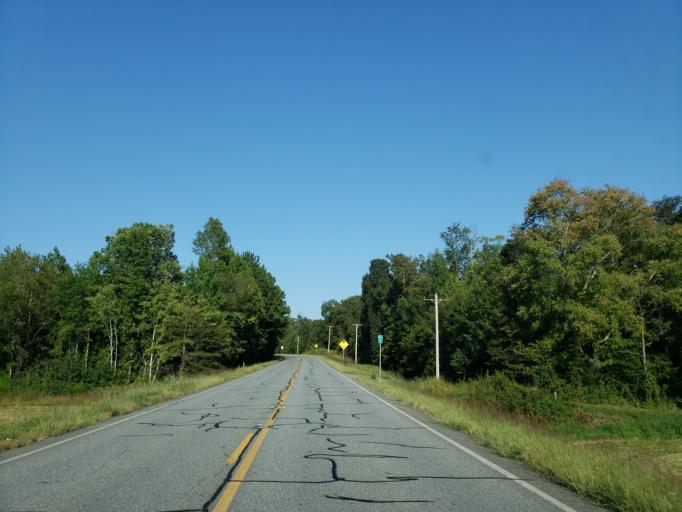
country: US
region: Georgia
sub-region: Whitfield County
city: Varnell
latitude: 34.9087
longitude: -84.8721
